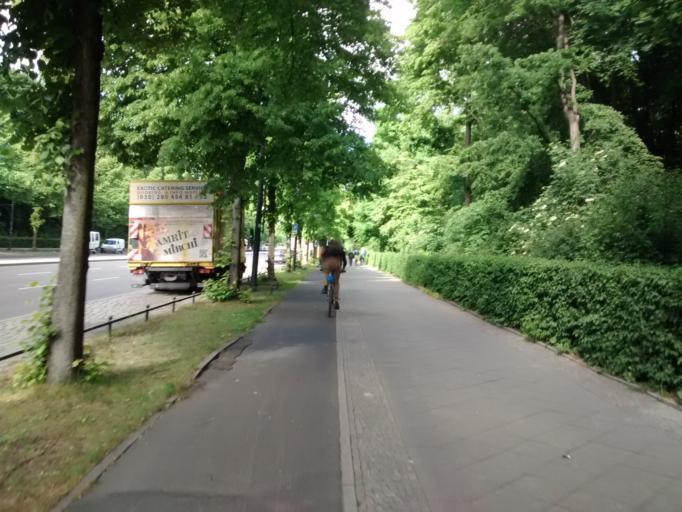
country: DE
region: Berlin
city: Tiergarten Bezirk
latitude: 52.5150
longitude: 13.3566
